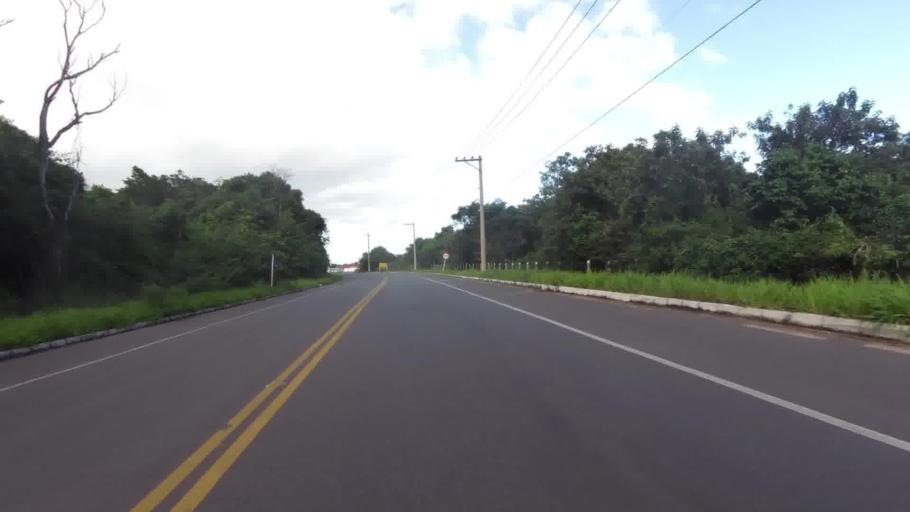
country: BR
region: Espirito Santo
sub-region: Piuma
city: Piuma
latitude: -20.8019
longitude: -40.6329
